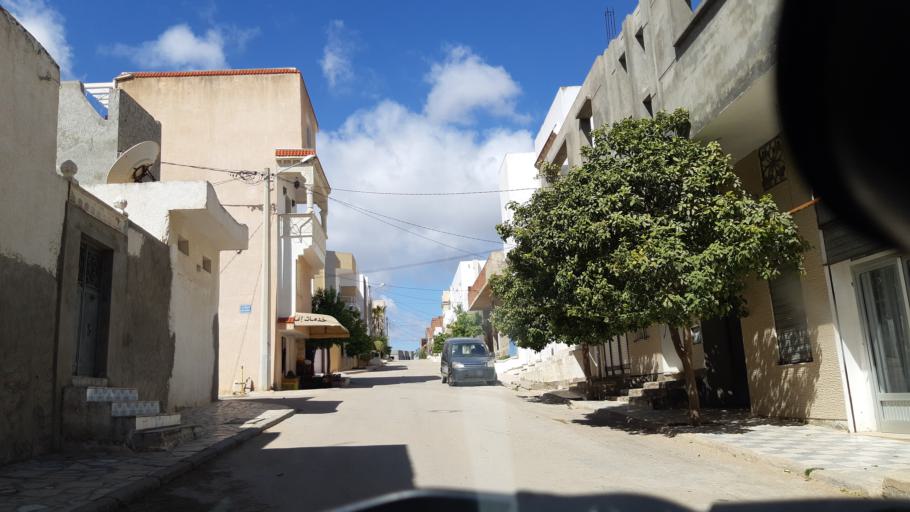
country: TN
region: Susah
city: Akouda
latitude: 35.8929
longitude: 10.5330
